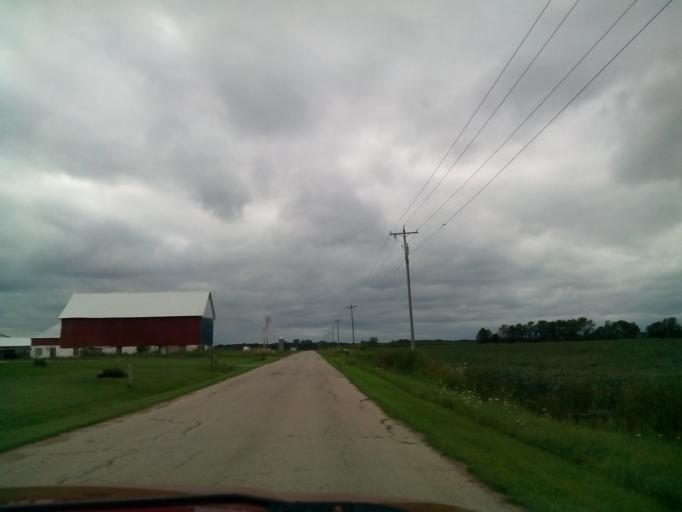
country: US
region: Wisconsin
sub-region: Outagamie County
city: Black Creek
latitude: 44.5237
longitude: -88.4566
